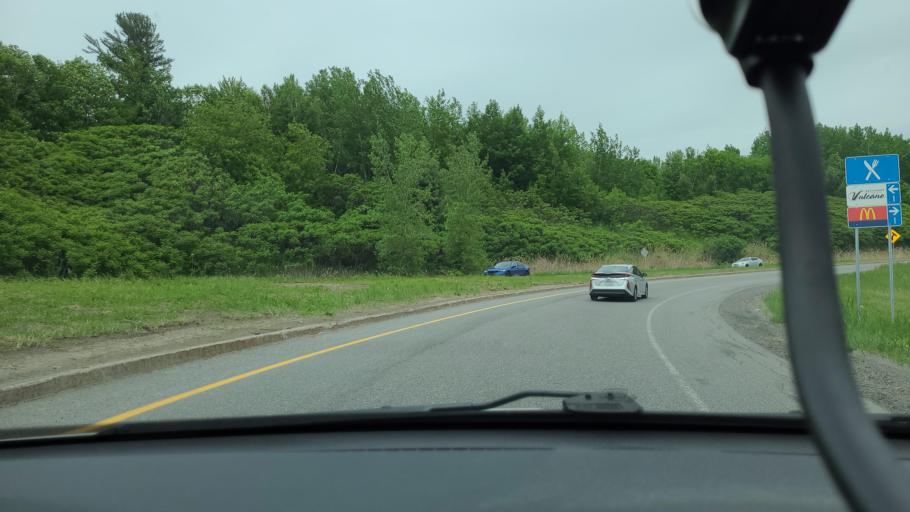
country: CA
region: Quebec
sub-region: Lanaudiere
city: Lorraine
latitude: 45.6728
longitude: -73.7684
